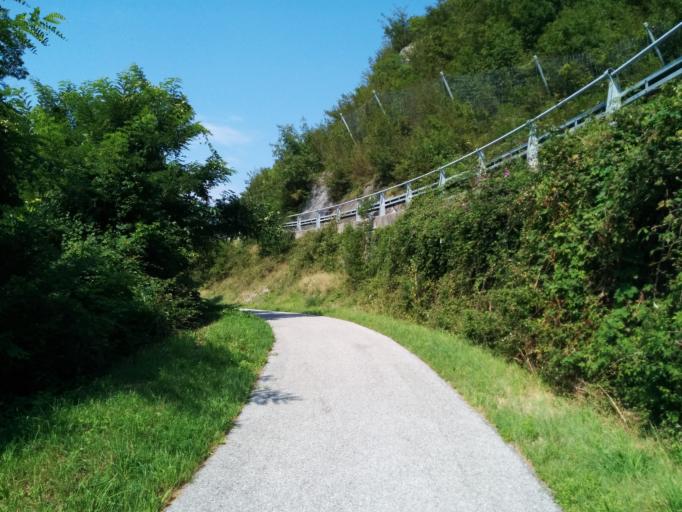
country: IT
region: Friuli Venezia Giulia
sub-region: Provincia di Udine
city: Villa Santina
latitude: 46.4221
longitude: 12.9085
